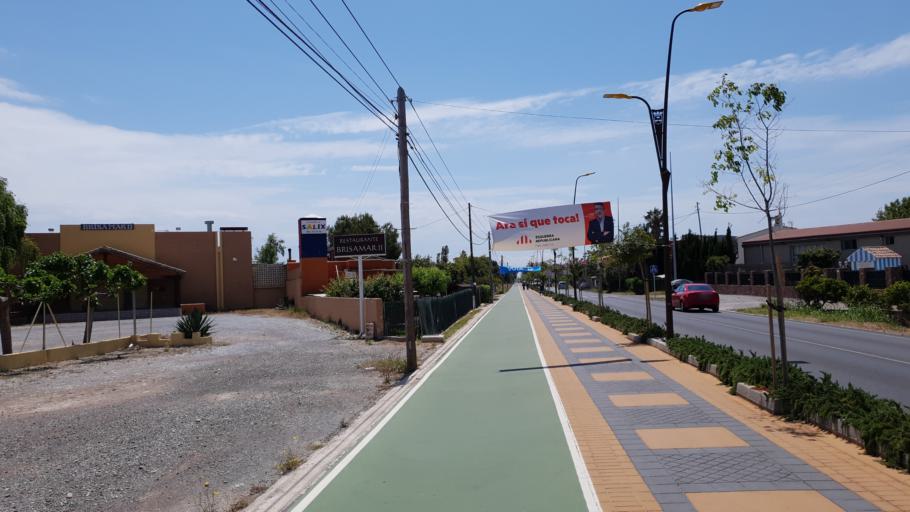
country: ES
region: Valencia
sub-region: Provincia de Castello
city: Burriana
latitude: 39.8766
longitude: -0.0773
